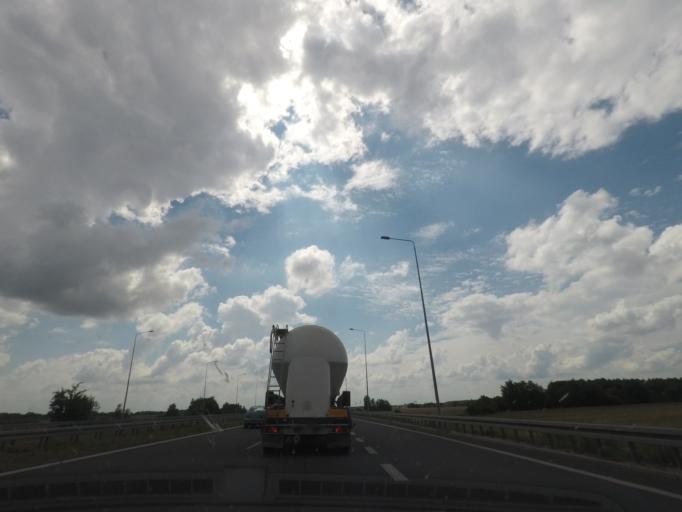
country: PL
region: Lodz Voivodeship
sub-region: Powiat leczycki
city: Piatek
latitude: 52.0027
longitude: 19.5448
